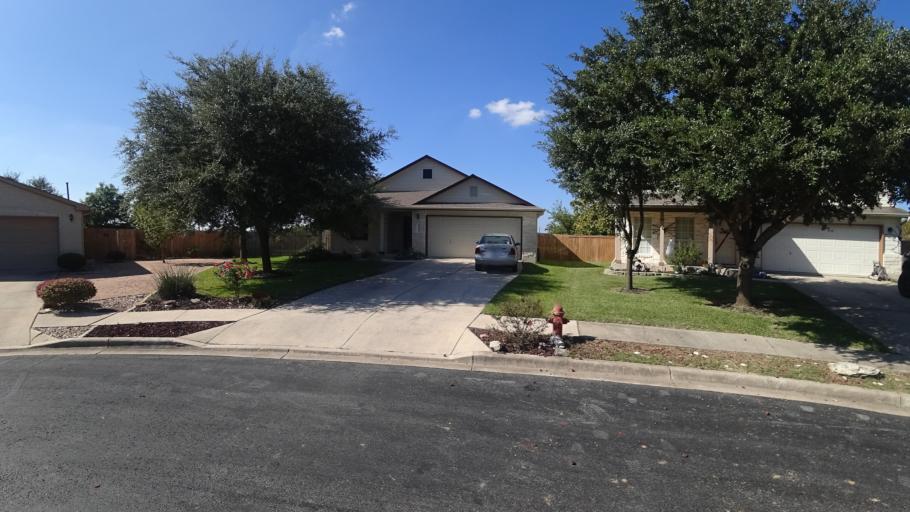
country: US
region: Texas
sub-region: Travis County
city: Manor
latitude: 30.3648
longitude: -97.6127
